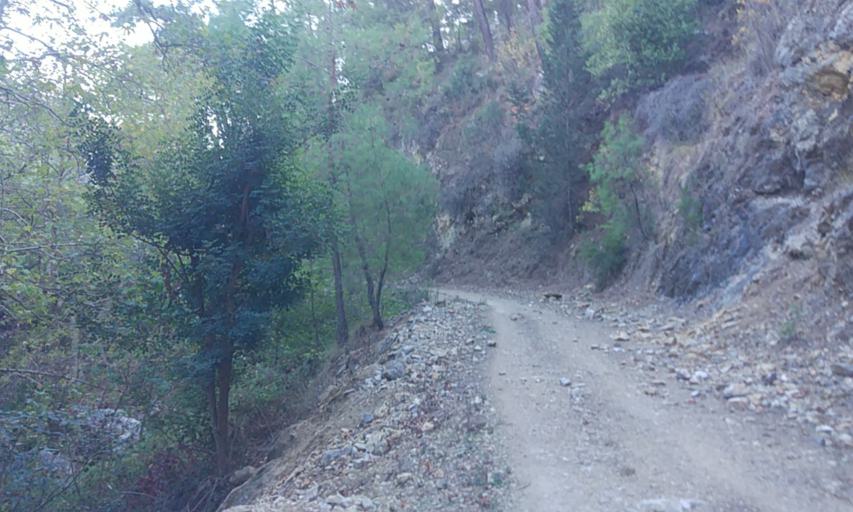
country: TR
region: Antalya
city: Tekirova
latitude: 36.4398
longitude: 30.4408
